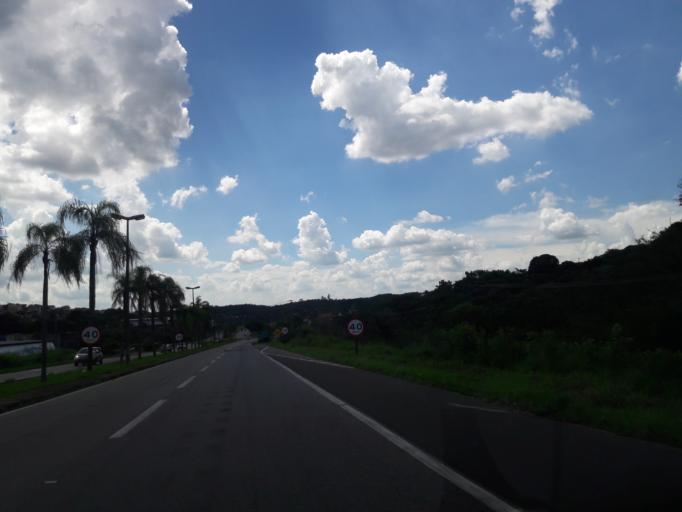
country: BR
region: Sao Paulo
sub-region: Campo Limpo Paulista
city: Campo Limpo Paulista
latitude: -23.2110
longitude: -46.7923
